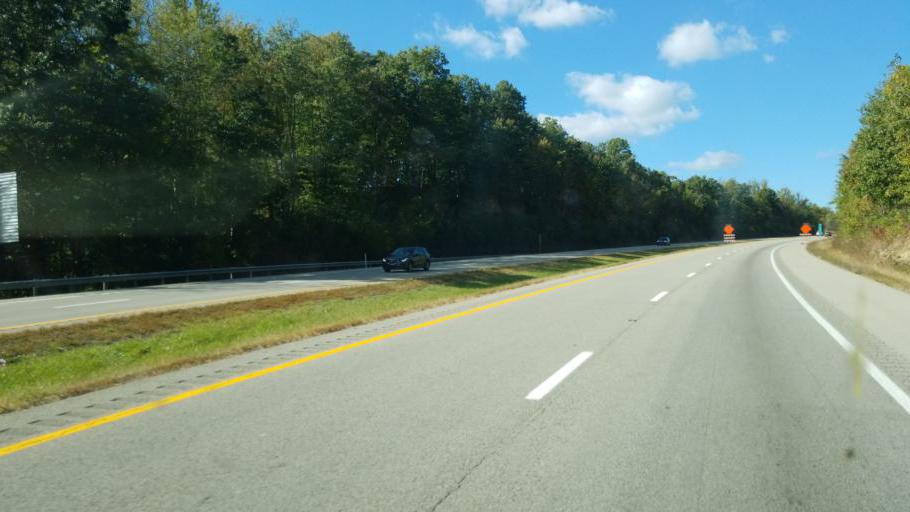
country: US
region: West Virginia
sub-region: Monongalia County
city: Star City
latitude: 39.6807
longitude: -80.0388
